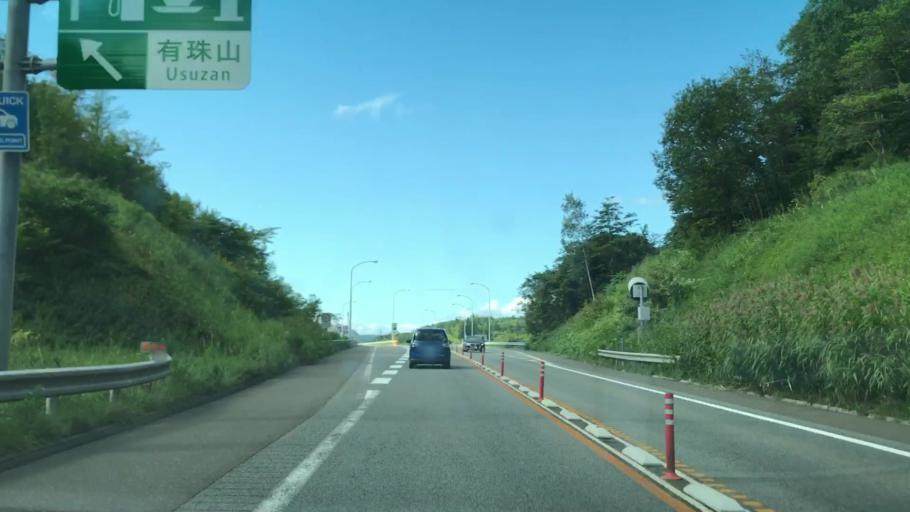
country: JP
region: Hokkaido
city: Date
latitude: 42.4621
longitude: 140.9107
